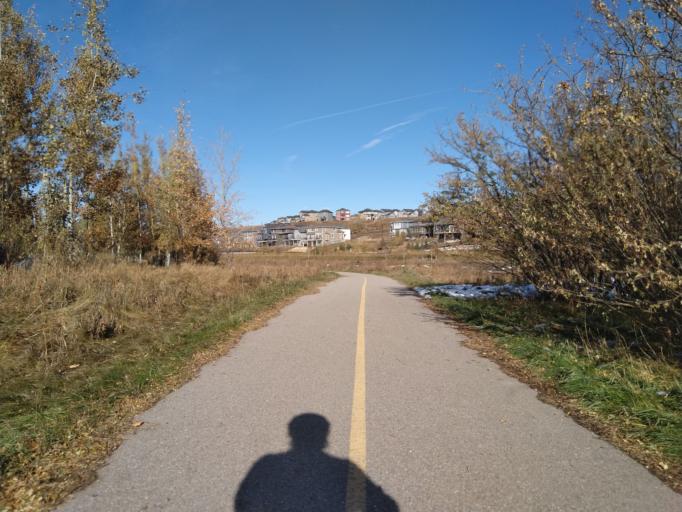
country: CA
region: Alberta
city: Calgary
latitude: 51.1728
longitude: -114.1282
